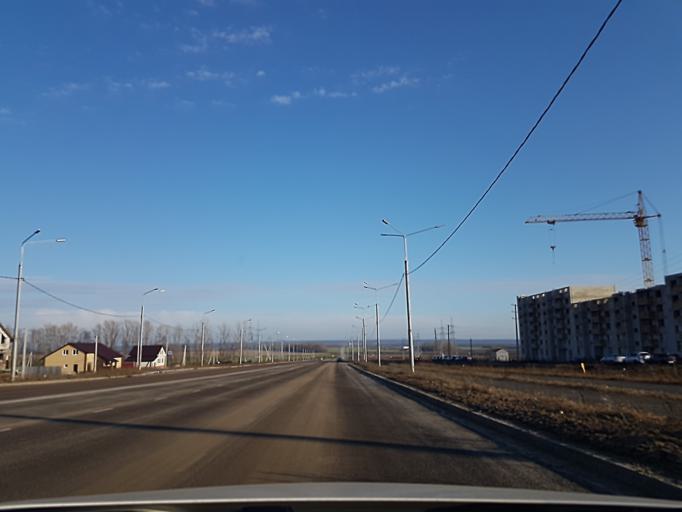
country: RU
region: Tambov
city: Tambov
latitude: 52.7842
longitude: 41.4175
